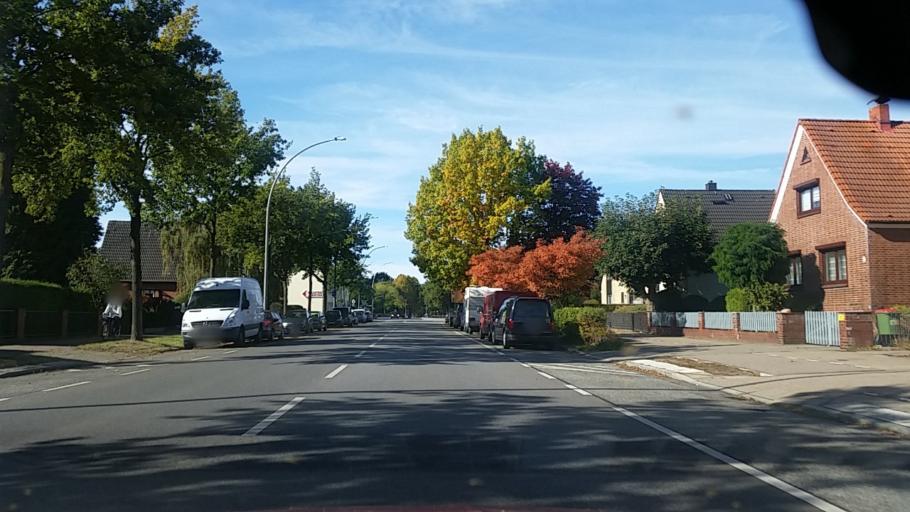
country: DE
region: Hamburg
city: Wandsbek
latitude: 53.5469
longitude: 10.1096
